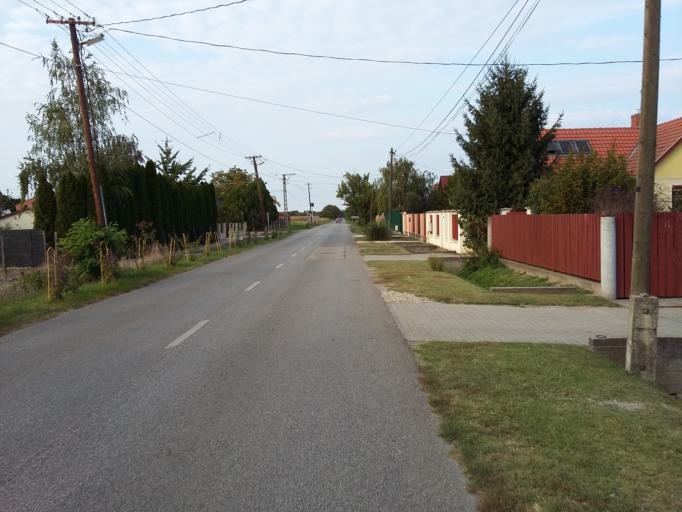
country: HU
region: Csongrad
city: Szeged
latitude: 46.2100
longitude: 20.1077
